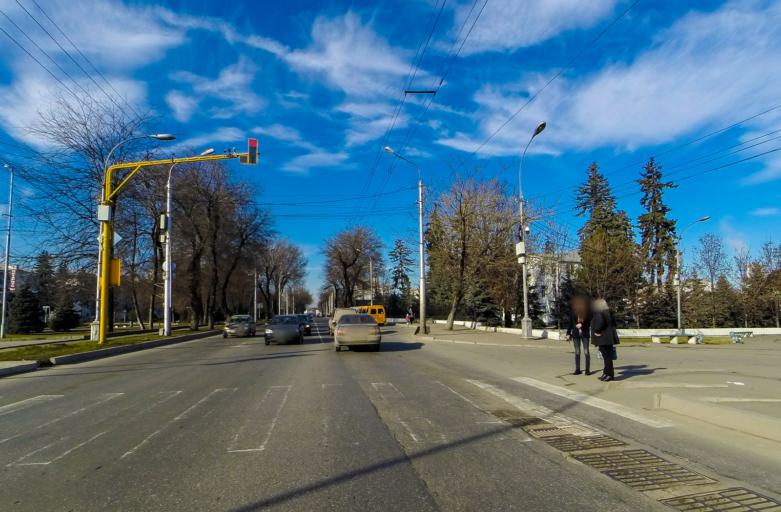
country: RU
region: Kabardino-Balkariya
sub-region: Gorod Nal'chik
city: Nal'chik
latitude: 43.4905
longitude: 43.6153
